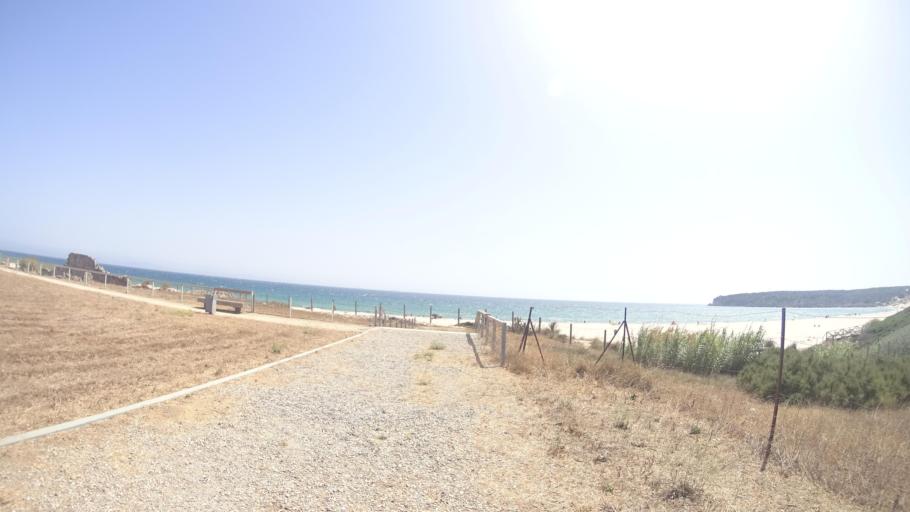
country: ES
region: Andalusia
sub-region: Provincia de Cadiz
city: Zahara de los Atunes
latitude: 36.0889
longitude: -5.7757
